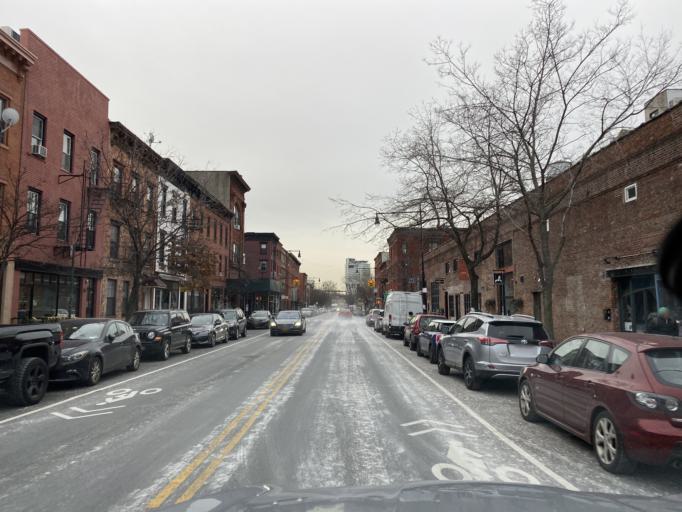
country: US
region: New York
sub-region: Queens County
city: Long Island City
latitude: 40.7306
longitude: -73.9577
